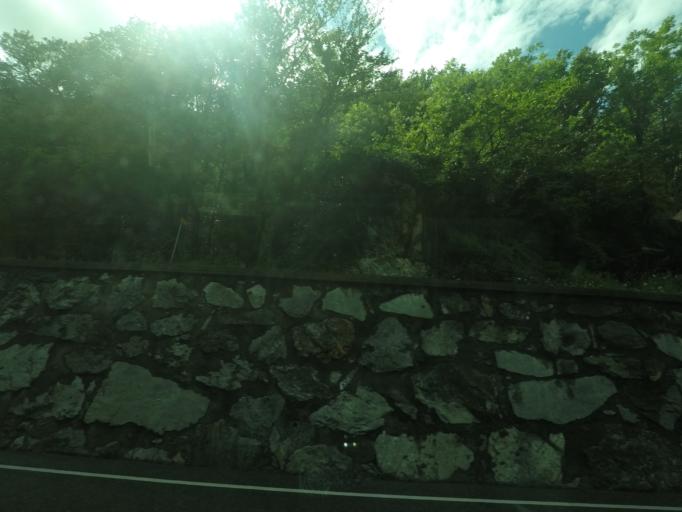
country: IT
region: Aosta Valley
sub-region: Valle d'Aosta
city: Chatillon
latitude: 45.7613
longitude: 7.6071
